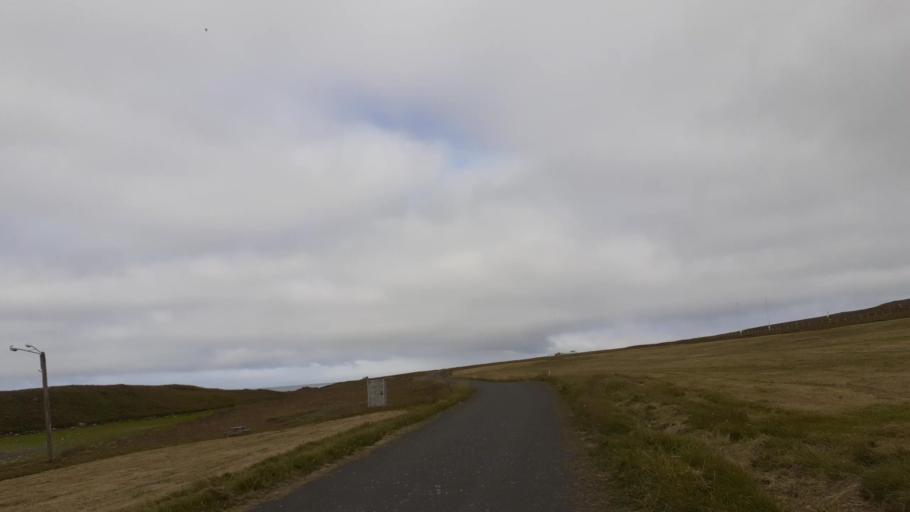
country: IS
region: Northeast
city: Dalvik
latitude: 66.5418
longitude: -18.0164
